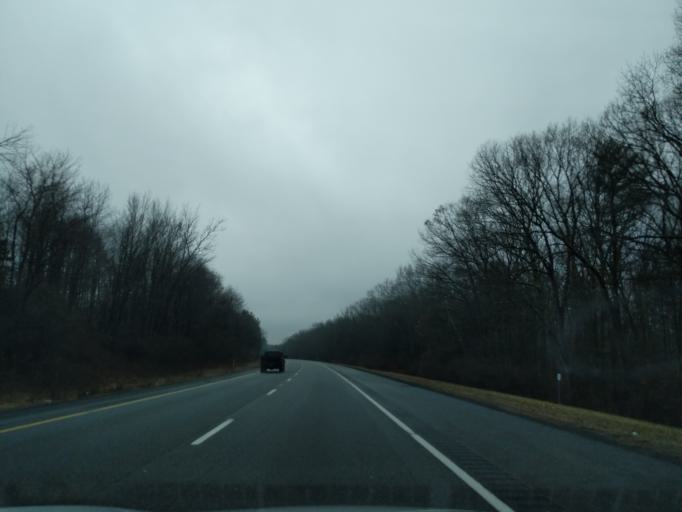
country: US
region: Massachusetts
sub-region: Worcester County
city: Oxford
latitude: 42.0946
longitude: -71.8632
